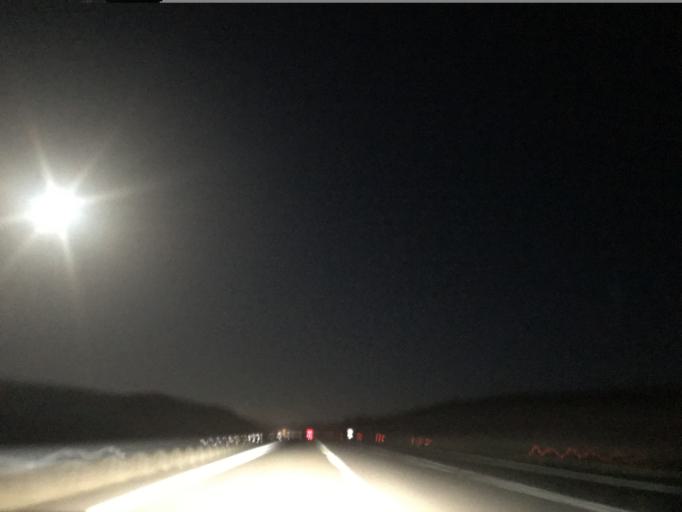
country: TR
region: Nigde
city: Ulukisla
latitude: 37.6434
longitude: 34.3753
